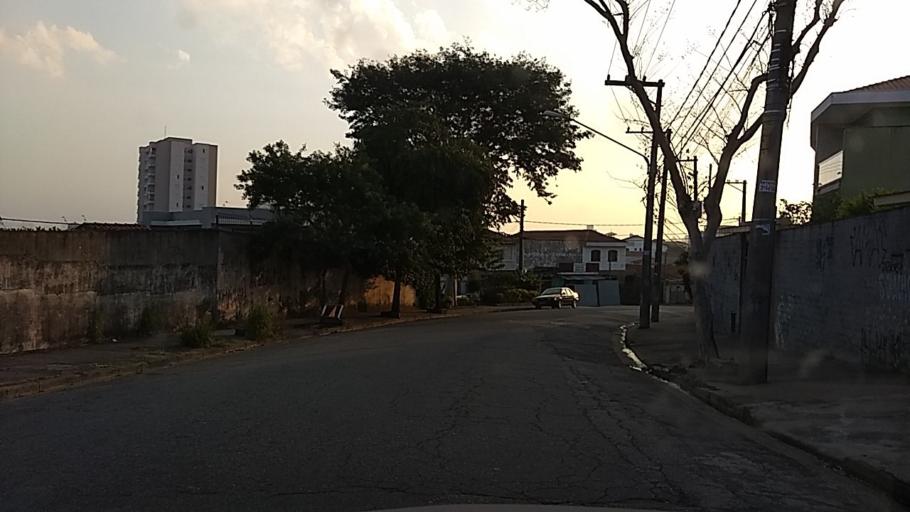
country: BR
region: Sao Paulo
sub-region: Sao Paulo
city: Sao Paulo
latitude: -23.5076
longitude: -46.5914
